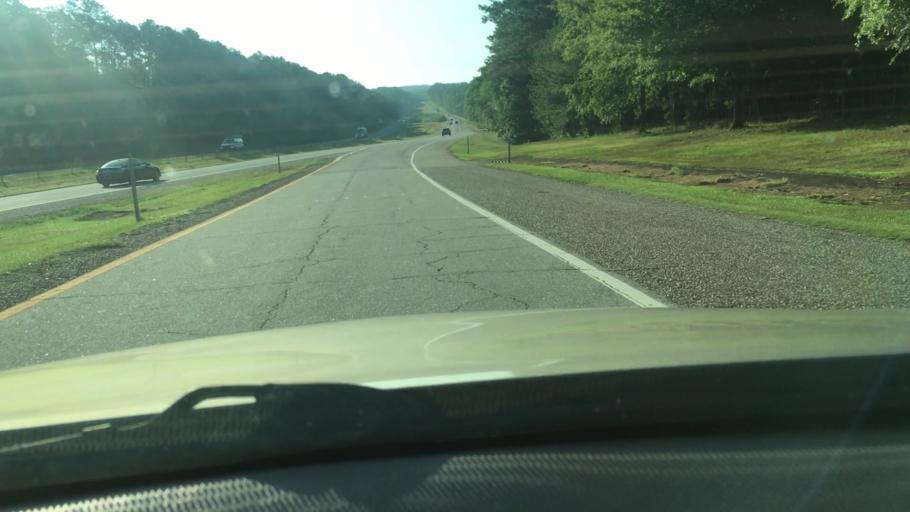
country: US
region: South Carolina
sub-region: Lexington County
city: Chapin
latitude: 34.1762
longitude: -81.3215
